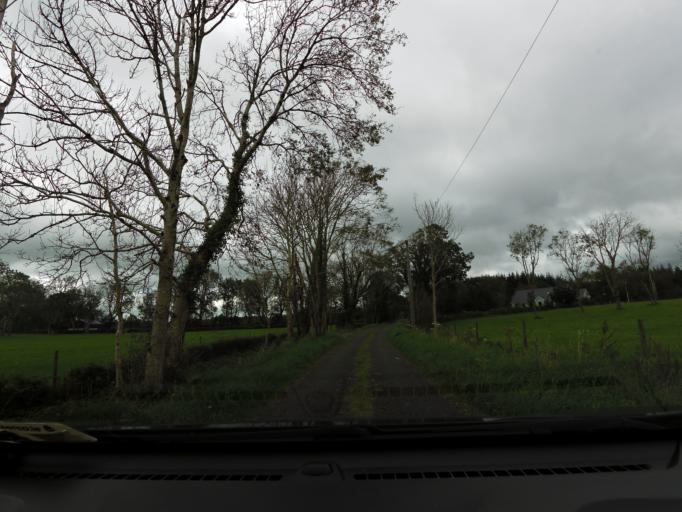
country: IE
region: Connaught
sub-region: County Galway
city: Athenry
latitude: 53.2990
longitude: -8.6676
